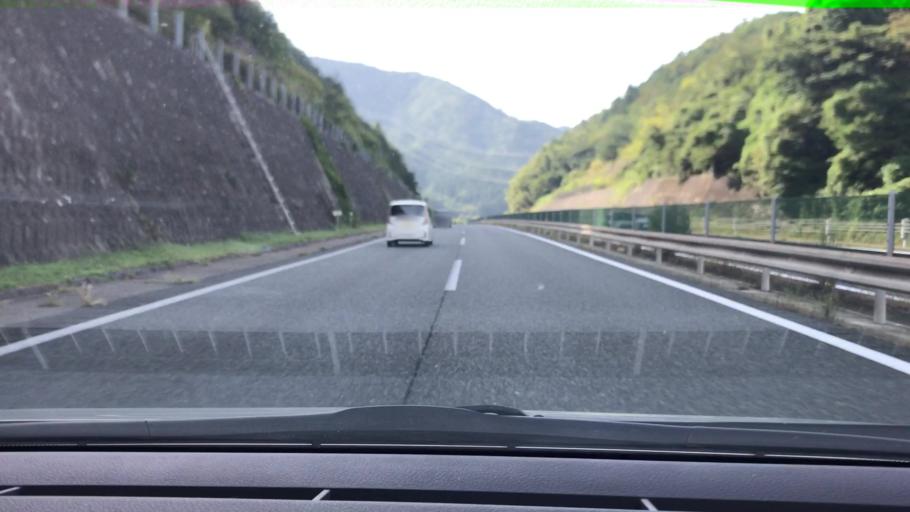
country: JP
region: Hyogo
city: Sasayama
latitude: 35.0425
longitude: 135.1824
